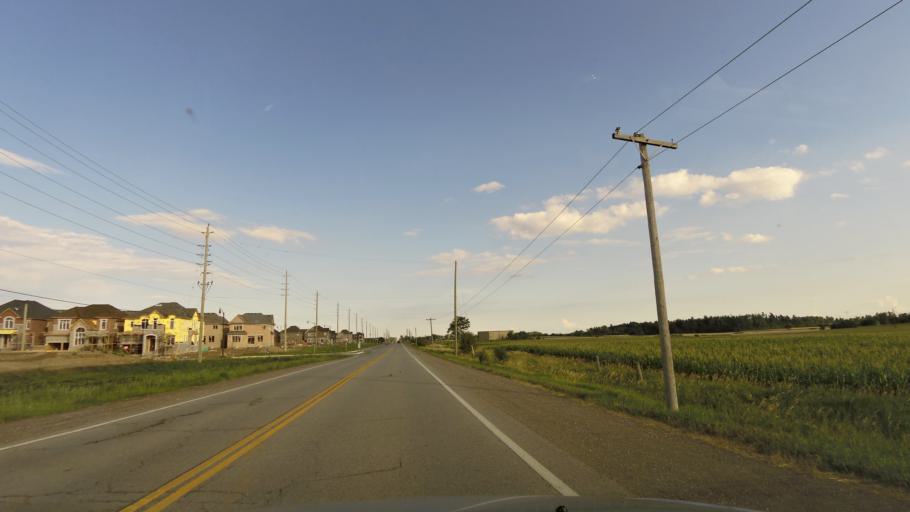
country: CA
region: Ontario
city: Brampton
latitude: 43.6844
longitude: -79.8534
